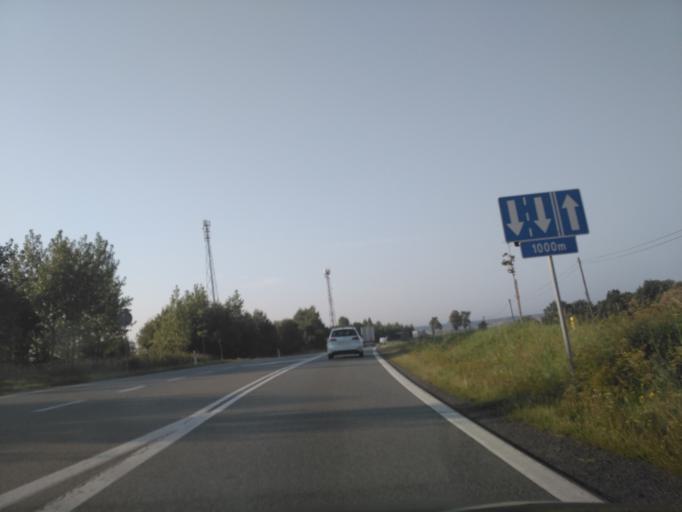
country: PL
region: Lublin Voivodeship
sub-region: Powiat janowski
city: Modliborzyce
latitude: 50.7704
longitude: 22.3254
